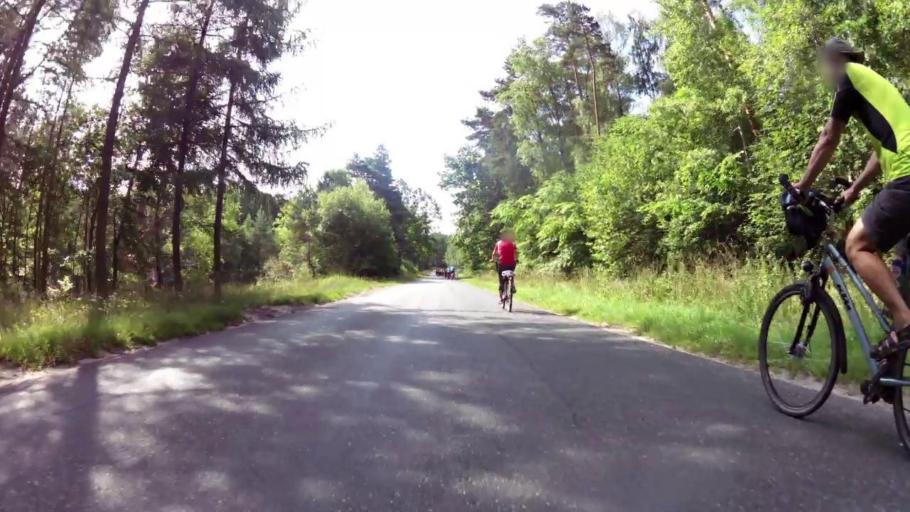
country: PL
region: West Pomeranian Voivodeship
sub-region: Powiat drawski
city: Drawsko Pomorskie
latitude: 53.4803
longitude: 15.7767
